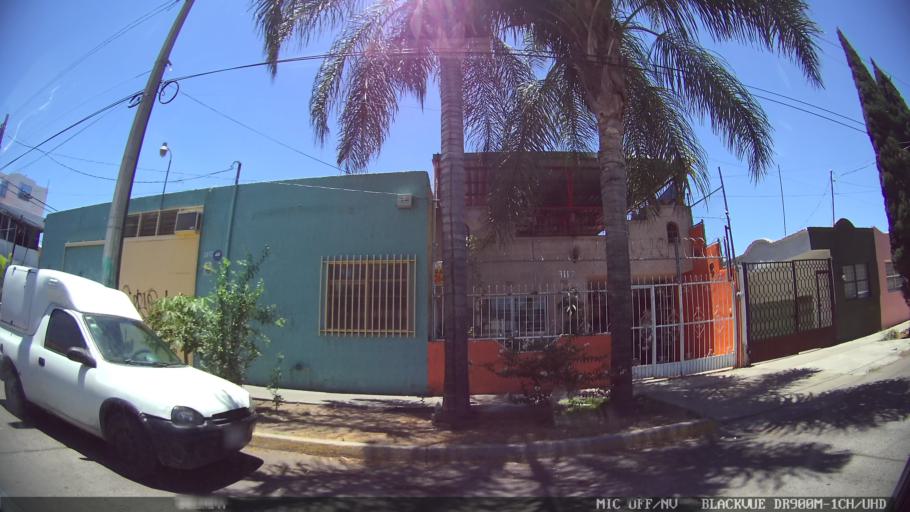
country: MX
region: Jalisco
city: Tlaquepaque
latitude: 20.6620
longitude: -103.2944
